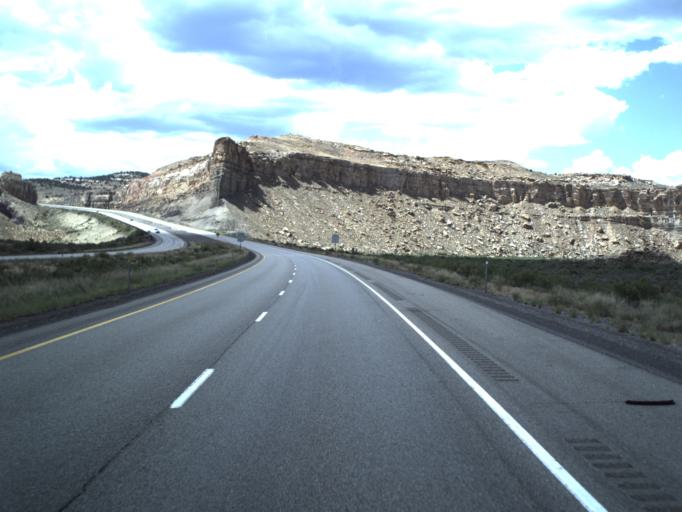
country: US
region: Utah
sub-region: Emery County
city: Ferron
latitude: 38.8098
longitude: -111.2523
